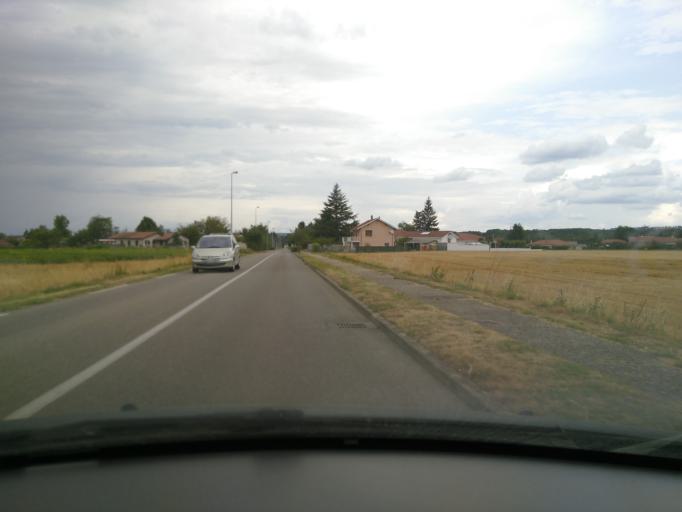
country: FR
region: Rhone-Alpes
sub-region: Departement de l'Isere
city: Beaurepaire
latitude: 45.3481
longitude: 5.0404
